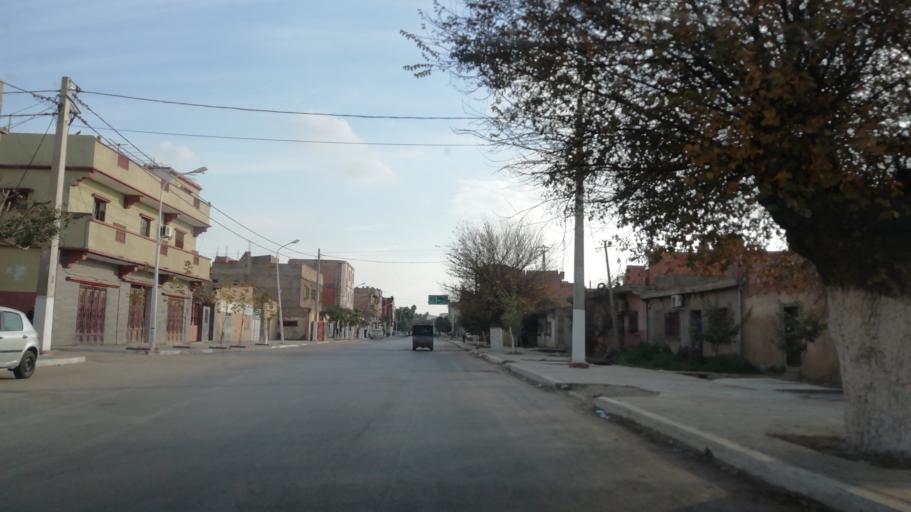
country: DZ
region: Mascara
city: Mascara
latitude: 35.5981
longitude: 0.0641
